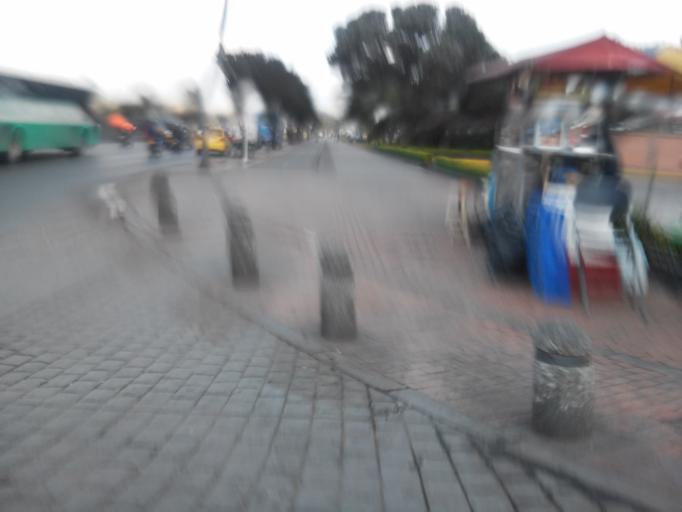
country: CO
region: Cundinamarca
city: Soacha
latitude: 4.5953
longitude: -74.1508
